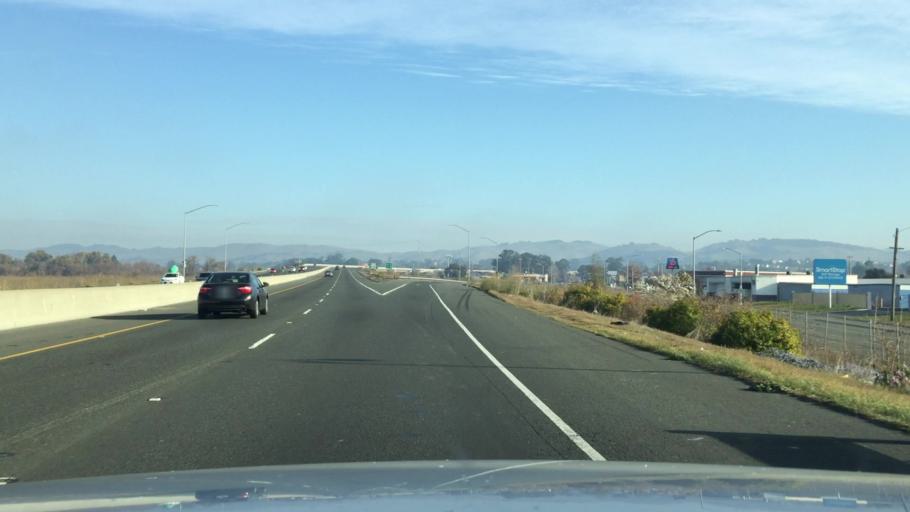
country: US
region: California
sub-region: Solano County
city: Vallejo
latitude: 38.1345
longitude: -122.2599
